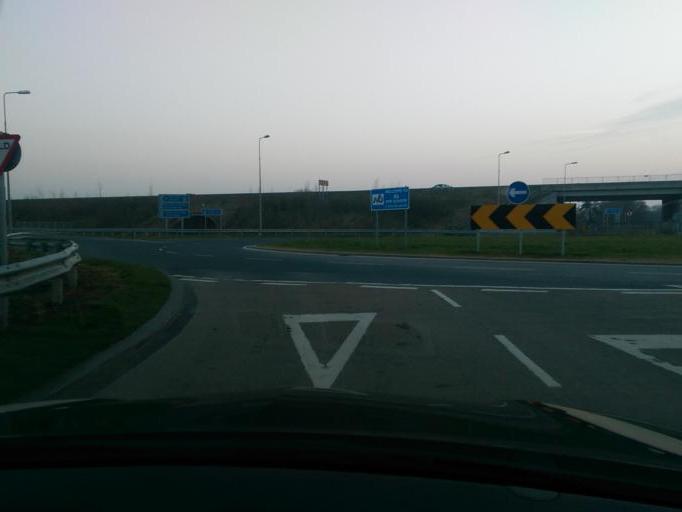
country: IE
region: Connaught
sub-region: County Galway
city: Athenry
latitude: 53.2880
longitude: -8.7596
